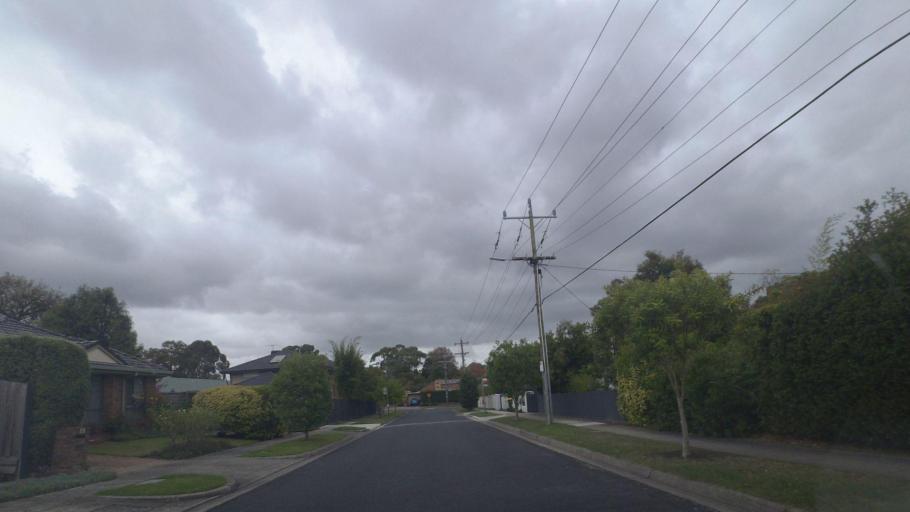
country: AU
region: Victoria
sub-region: Whitehorse
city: Nunawading
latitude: -37.8269
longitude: 145.1688
